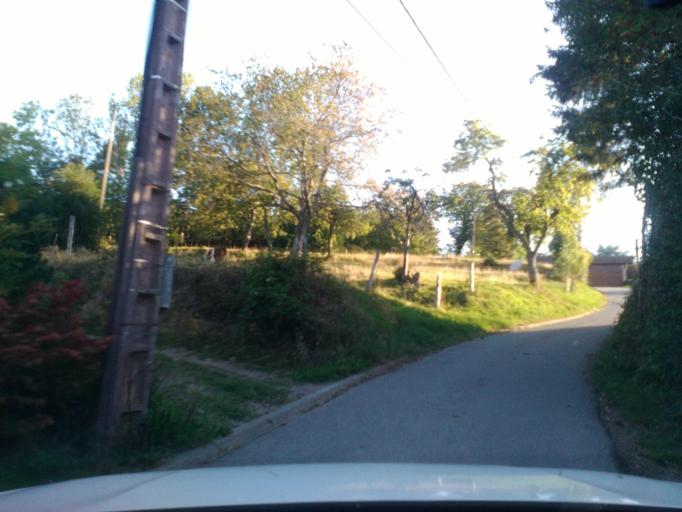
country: FR
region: Lorraine
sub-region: Departement des Vosges
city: Ban-de-Laveline
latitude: 48.3406
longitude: 7.0687
